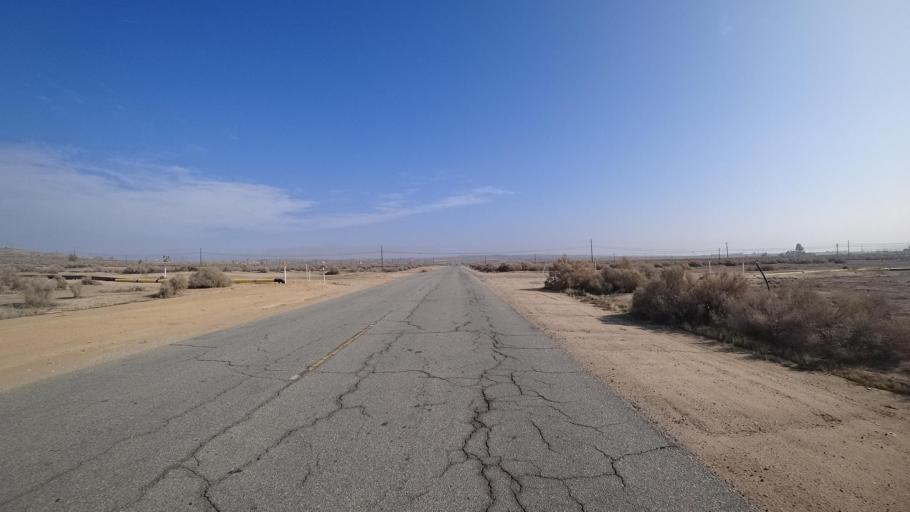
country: US
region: California
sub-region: Kern County
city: Ford City
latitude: 35.1546
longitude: -119.4318
